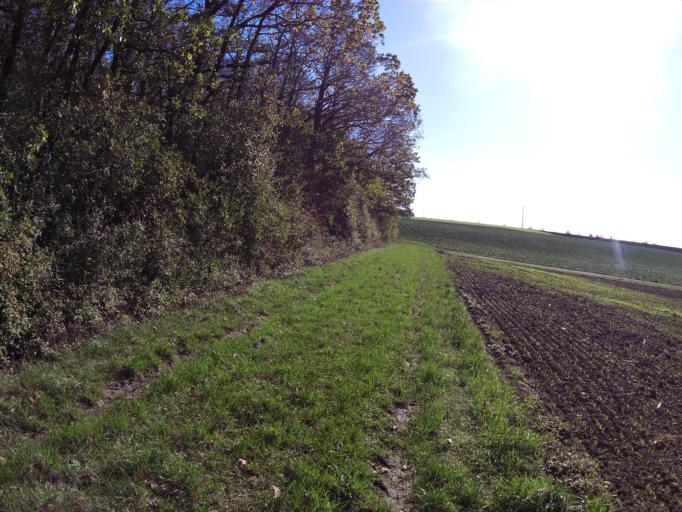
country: DE
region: Bavaria
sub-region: Regierungsbezirk Unterfranken
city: Sulzfeld am Main
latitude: 49.7110
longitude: 10.0936
